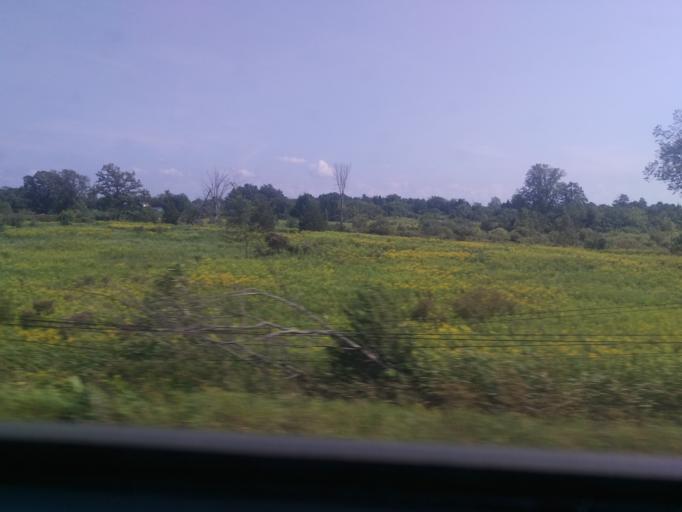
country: US
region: New York
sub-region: Jefferson County
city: Alexandria Bay
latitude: 44.4693
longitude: -75.8975
